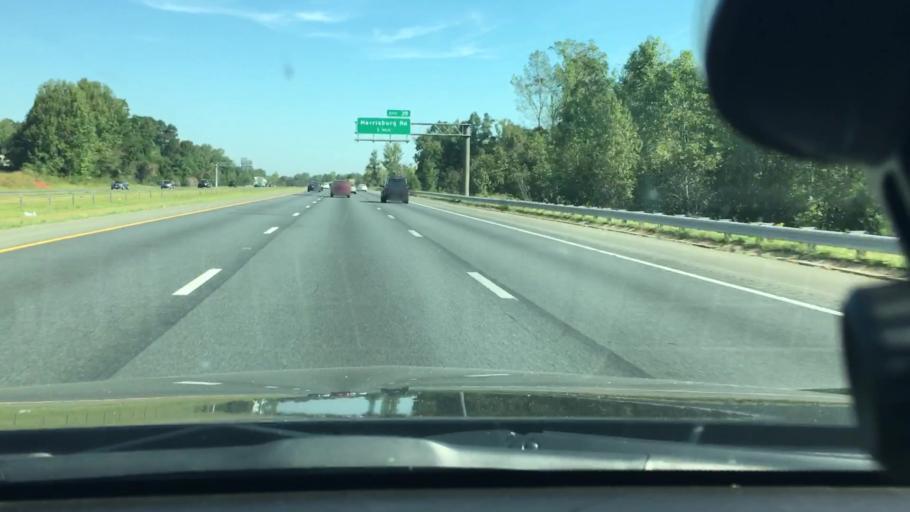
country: US
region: North Carolina
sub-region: Mecklenburg County
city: Mint Hill
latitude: 35.2350
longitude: -80.6530
